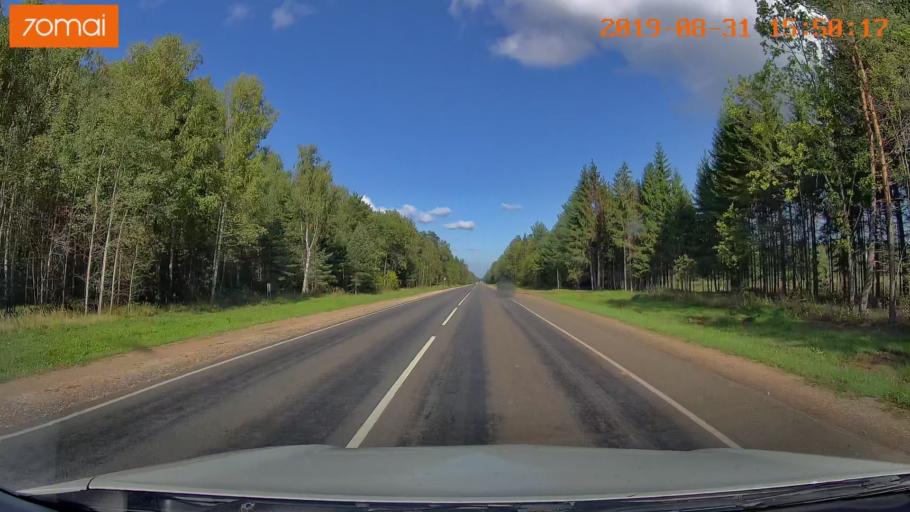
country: RU
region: Kaluga
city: Yukhnov
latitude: 54.6963
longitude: 35.0700
